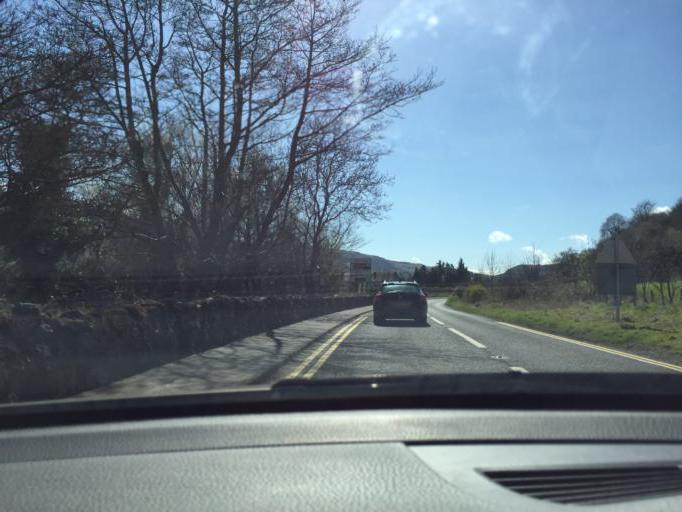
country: GB
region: Northern Ireland
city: Glenariff
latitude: 55.0633
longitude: -6.0597
